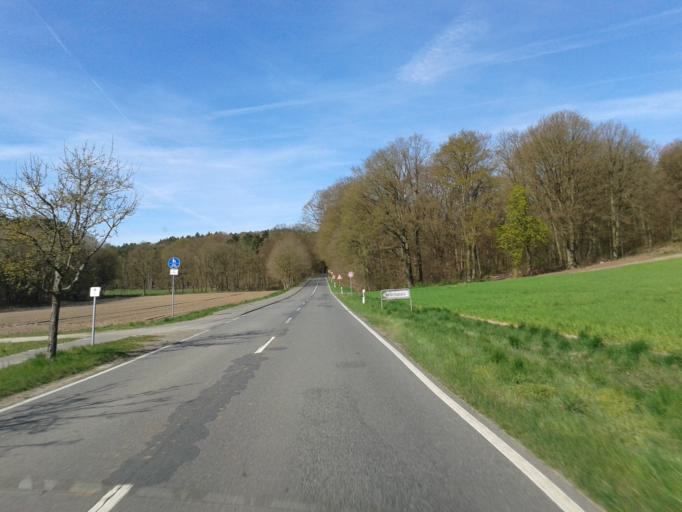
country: DE
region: Lower Saxony
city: Clenze
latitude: 52.9309
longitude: 10.9201
